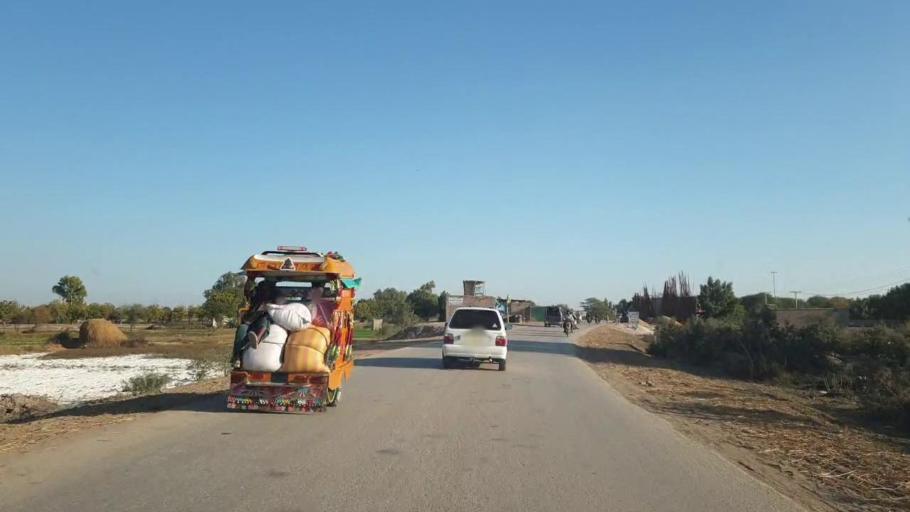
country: PK
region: Sindh
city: Dokri
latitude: 27.3668
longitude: 68.1117
